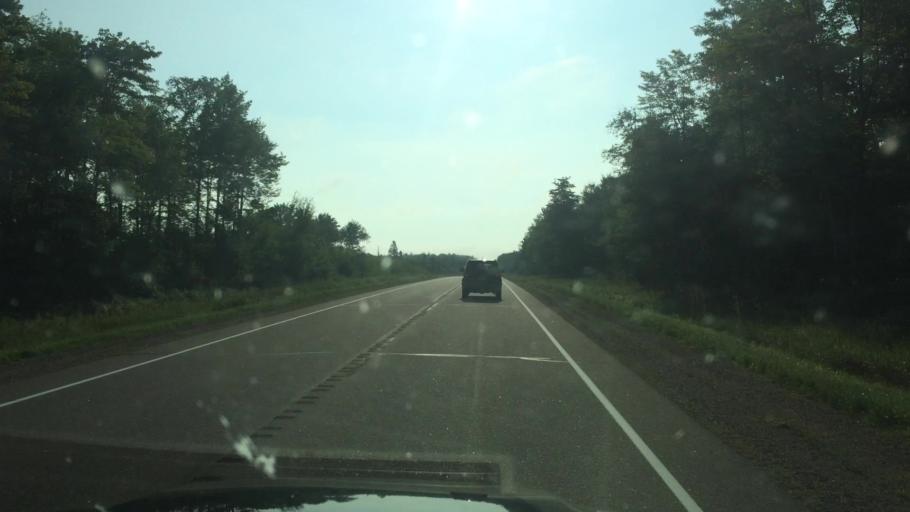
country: US
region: Wisconsin
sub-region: Langlade County
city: Antigo
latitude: 45.1469
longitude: -89.3760
